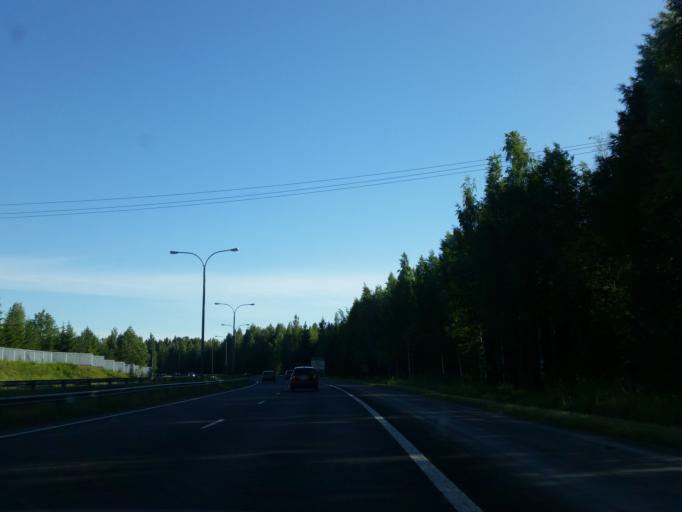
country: FI
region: Northern Savo
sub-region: Kuopio
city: Kuopio
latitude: 62.8768
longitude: 27.6242
